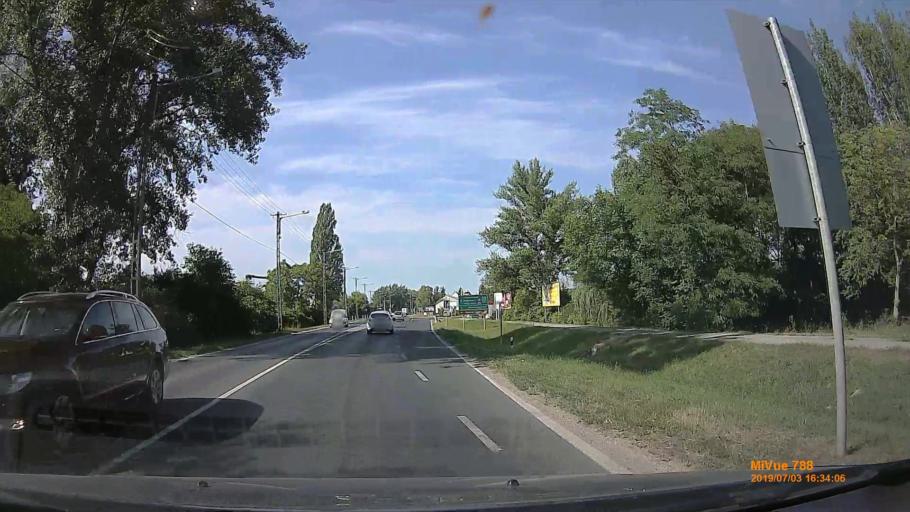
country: HU
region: Gyor-Moson-Sopron
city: Gyor
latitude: 47.7045
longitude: 17.6336
